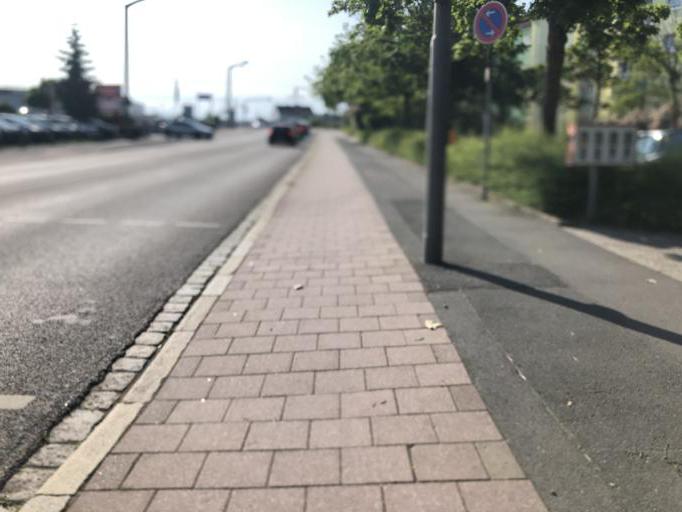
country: DE
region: Bavaria
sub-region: Regierungsbezirk Mittelfranken
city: Erlangen
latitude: 49.5736
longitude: 10.9958
